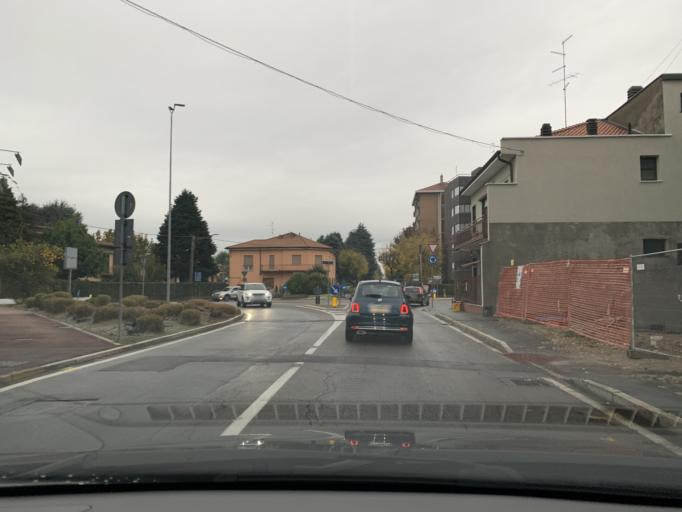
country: IT
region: Lombardy
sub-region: Provincia di Varese
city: Saronno
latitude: 45.6289
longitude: 9.0463
